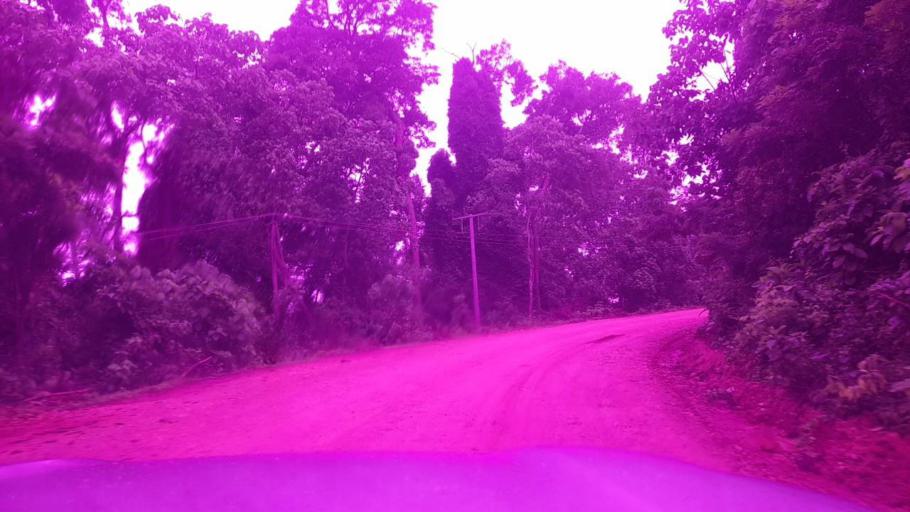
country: ET
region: Southern Nations, Nationalities, and People's Region
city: Bonga
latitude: 7.5041
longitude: 36.1008
